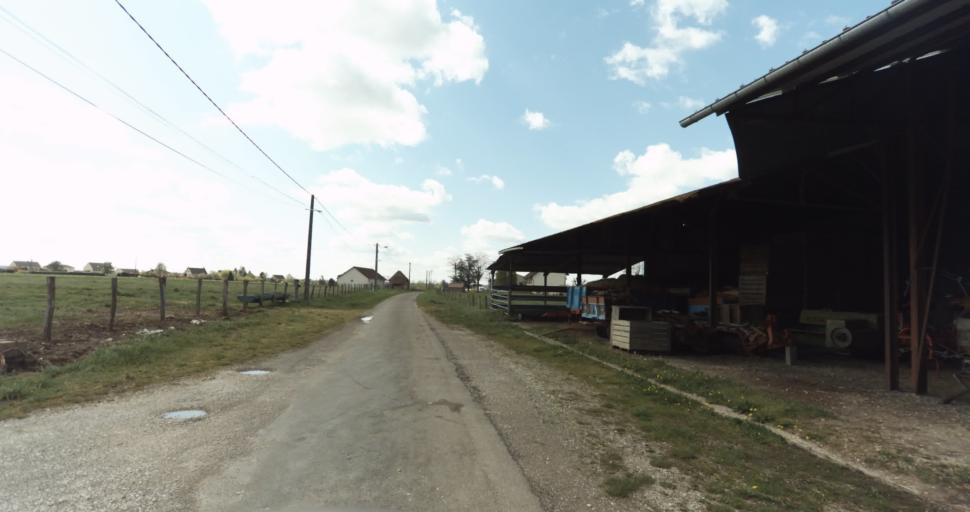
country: FR
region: Bourgogne
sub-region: Departement de la Cote-d'Or
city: Auxonne
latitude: 47.2166
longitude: 5.4188
